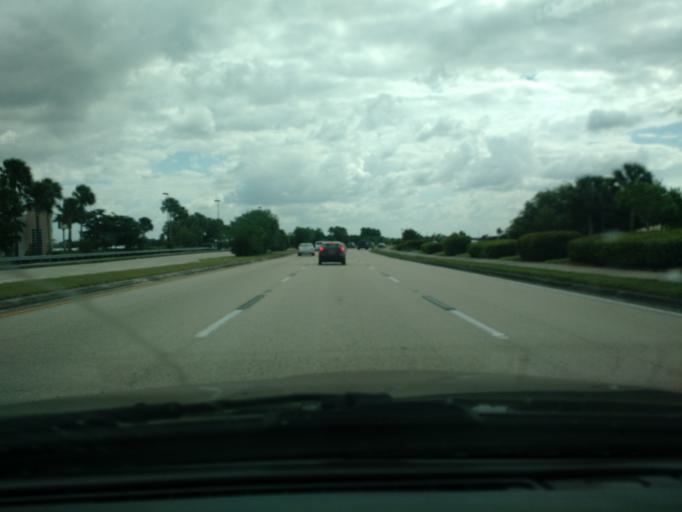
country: US
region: Florida
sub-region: Lee County
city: Pine Manor
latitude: 26.5876
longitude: -81.8689
